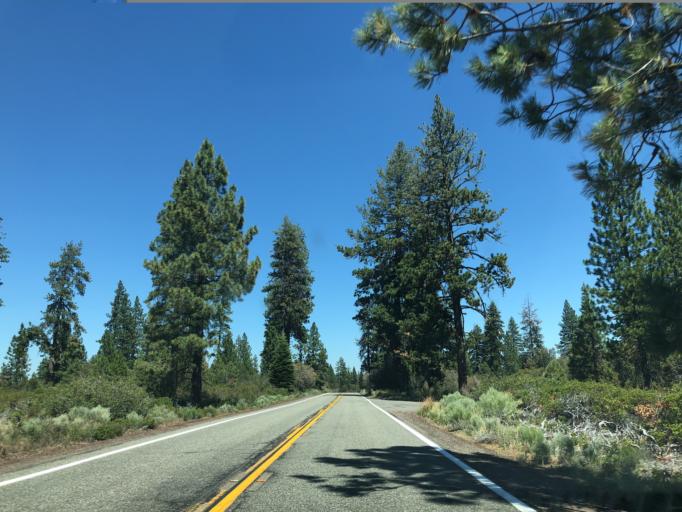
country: US
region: California
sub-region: Shasta County
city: Burney
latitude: 40.6167
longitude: -121.4990
